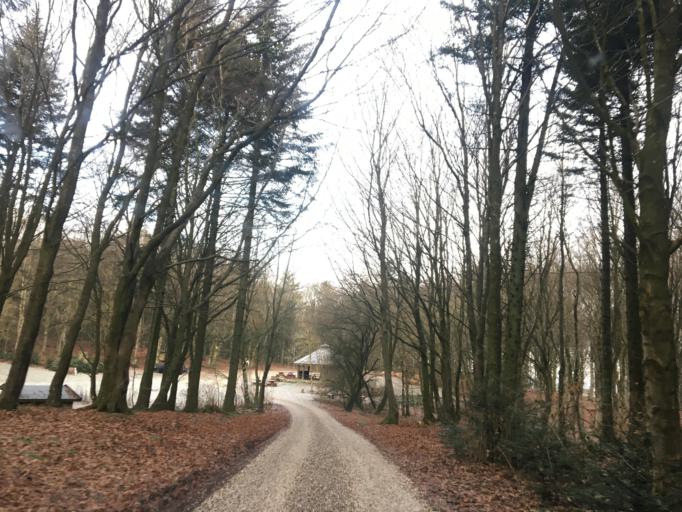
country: DK
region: North Denmark
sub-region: Thisted Kommune
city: Hurup
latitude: 56.7560
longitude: 8.3902
